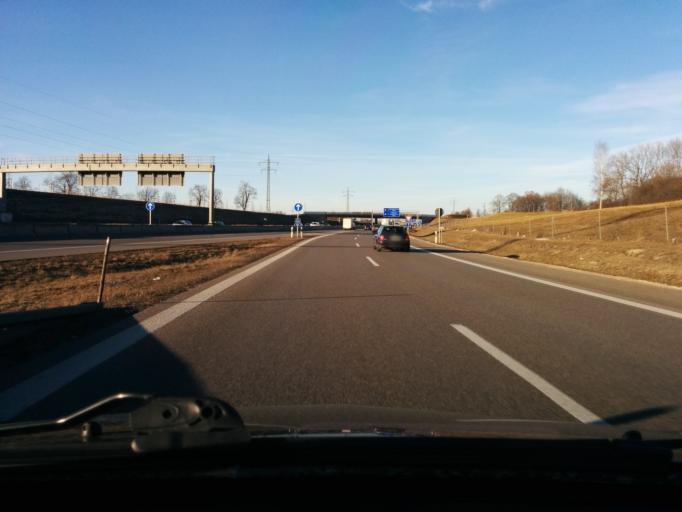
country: DE
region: Bavaria
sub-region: Upper Bavaria
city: Germering
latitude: 48.1308
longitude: 11.4024
